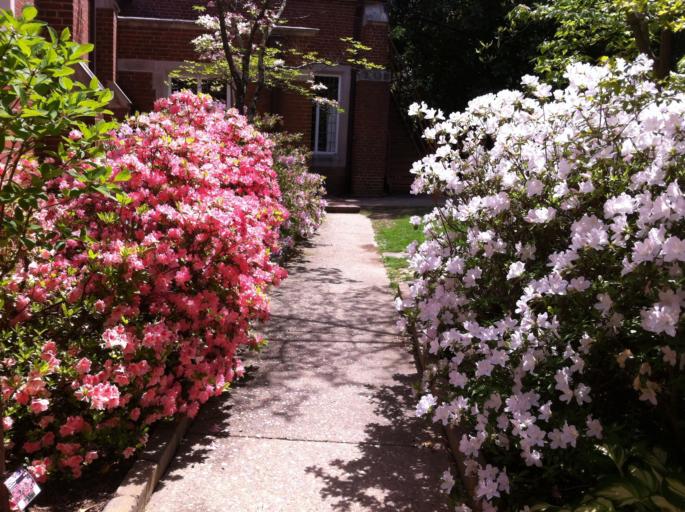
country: US
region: Virginia
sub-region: Henrico County
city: Dumbarton
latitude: 37.5760
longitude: -77.4982
